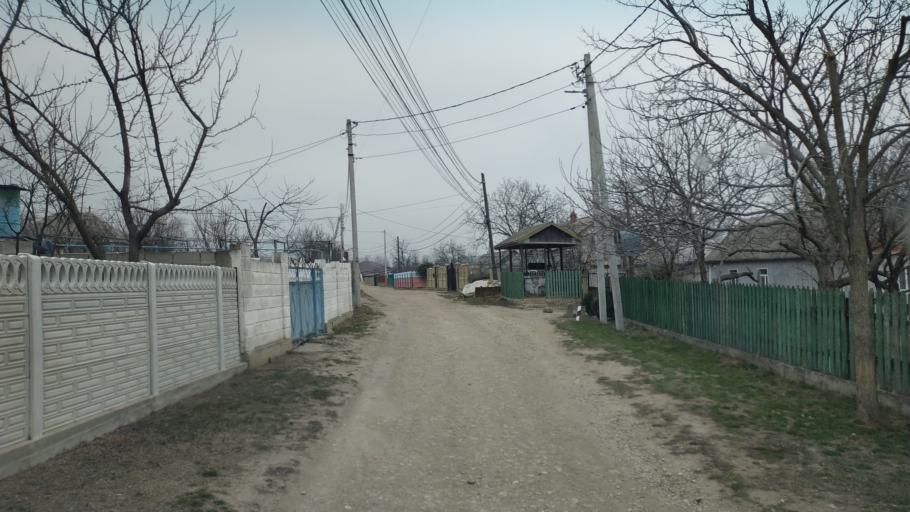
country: MD
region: Chisinau
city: Singera
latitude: 46.9118
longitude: 28.9400
